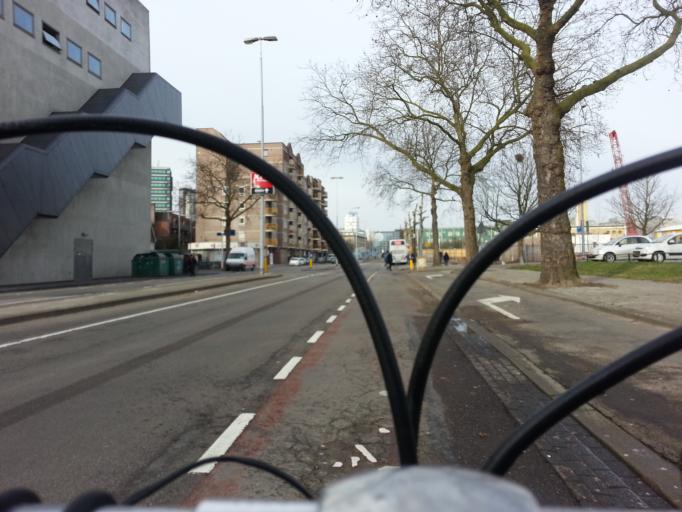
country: NL
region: North Brabant
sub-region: Gemeente Eindhoven
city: Eindhoven
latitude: 51.4422
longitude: 5.4837
